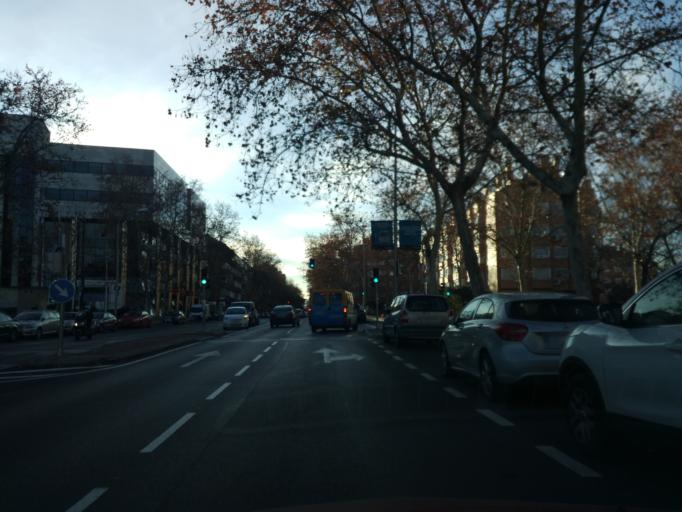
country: ES
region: Madrid
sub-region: Provincia de Madrid
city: San Blas
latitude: 40.4398
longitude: -3.6315
